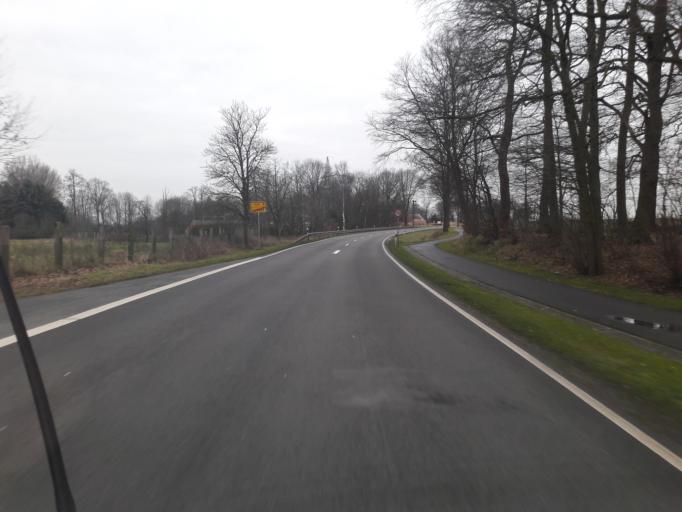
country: DE
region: Lower Saxony
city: Uchte
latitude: 52.4819
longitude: 8.8798
